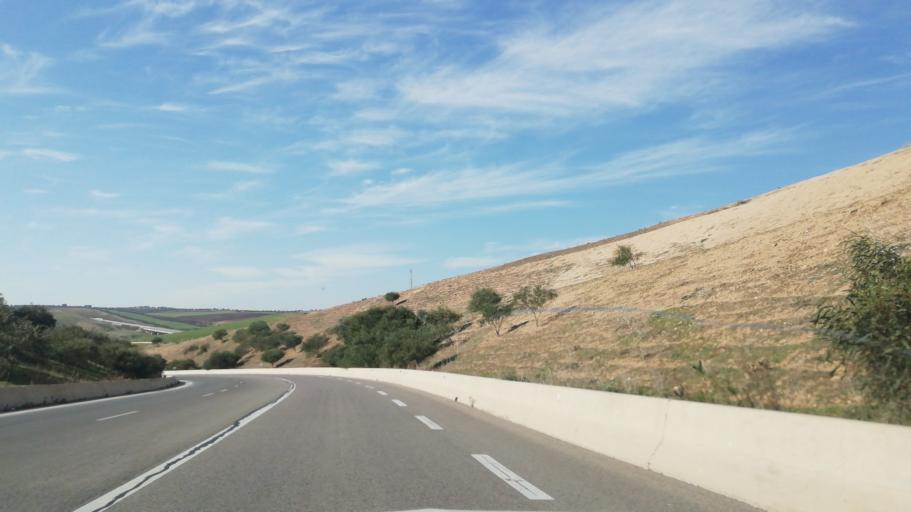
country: DZ
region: Tlemcen
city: Chetouane
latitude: 34.9819
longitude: -1.2282
